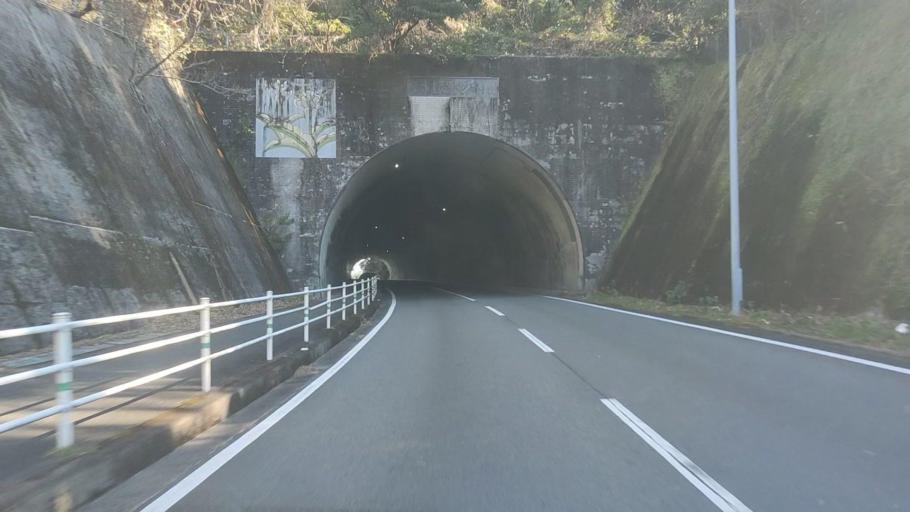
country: JP
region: Oita
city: Saiki
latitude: 32.8005
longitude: 131.9324
